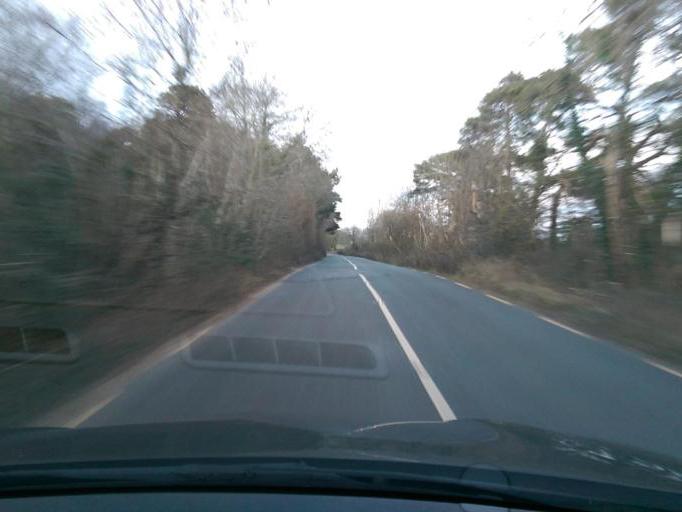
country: IE
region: Connaught
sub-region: County Galway
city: Portumna
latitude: 53.0688
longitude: -8.0852
